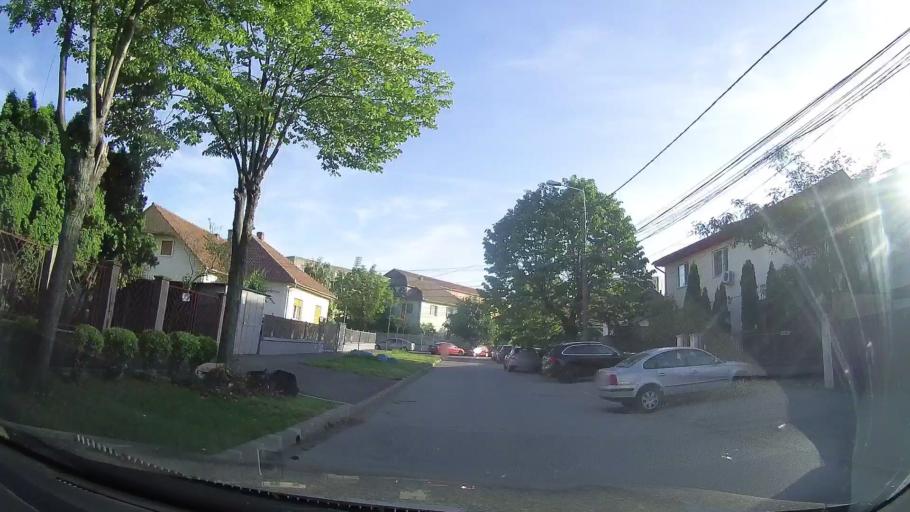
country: RO
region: Timis
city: Timisoara
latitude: 45.7446
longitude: 21.2464
